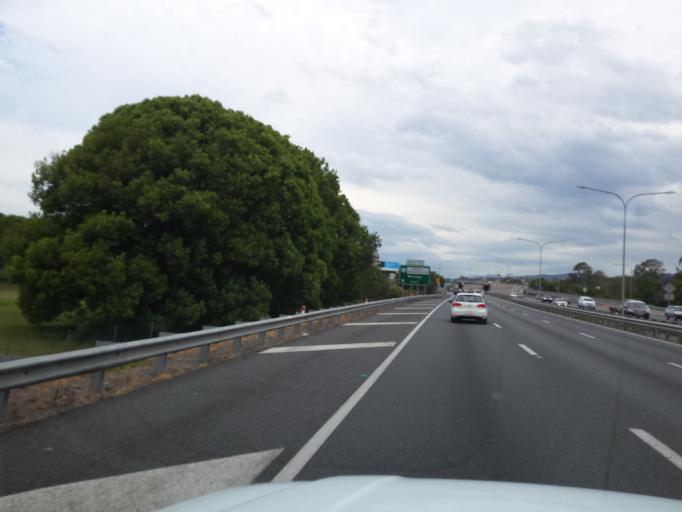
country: AU
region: Queensland
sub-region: Gold Coast
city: Nerang
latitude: -27.9895
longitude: 153.3408
